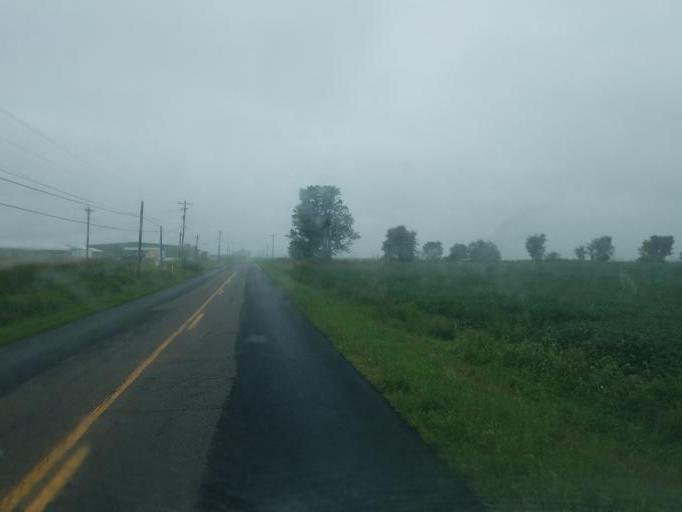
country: US
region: Ohio
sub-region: Licking County
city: Johnstown
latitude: 40.1850
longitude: -82.6926
